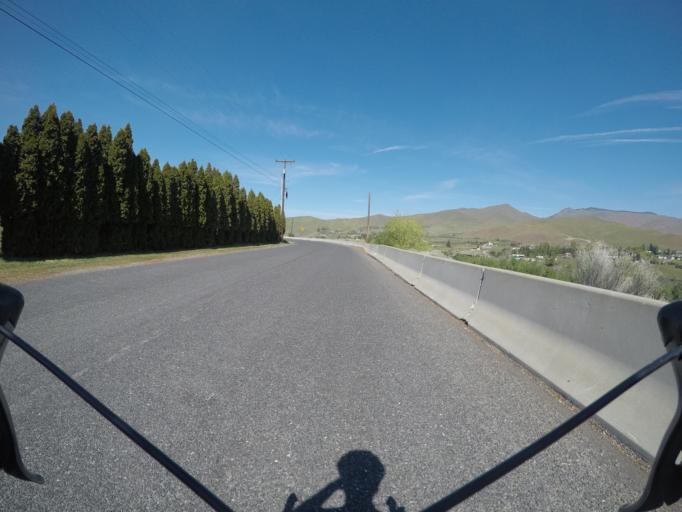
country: US
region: Washington
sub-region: Chelan County
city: West Wenatchee
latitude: 47.4768
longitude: -120.3830
